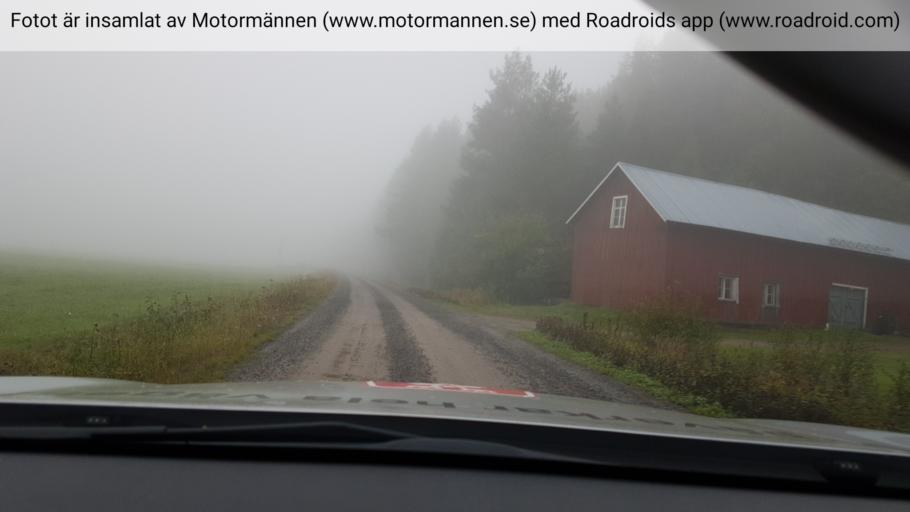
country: SE
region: Vaesterbotten
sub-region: Skelleftea Kommun
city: Burtraesk
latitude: 64.2972
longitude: 20.4262
